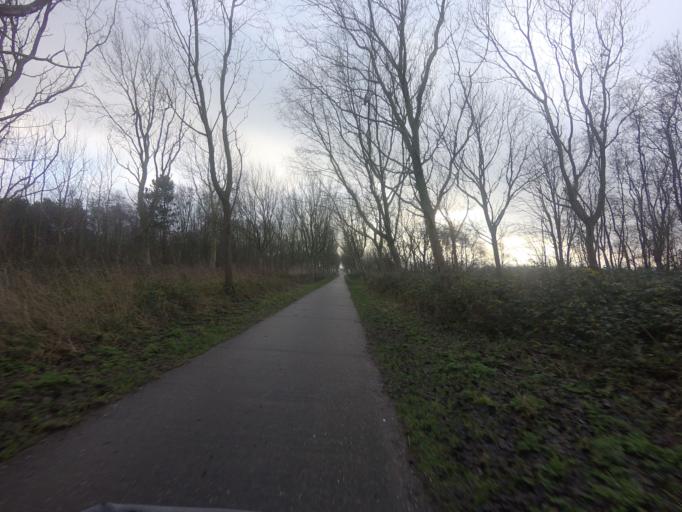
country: NL
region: North Holland
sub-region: Gemeente Texel
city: Den Burg
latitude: 53.1613
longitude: 4.8523
